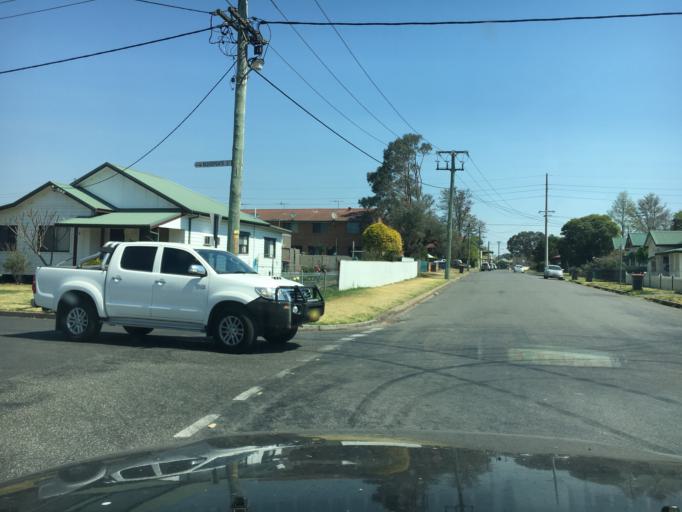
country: AU
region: New South Wales
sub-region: Singleton
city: Singleton
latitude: -32.5600
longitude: 151.1766
